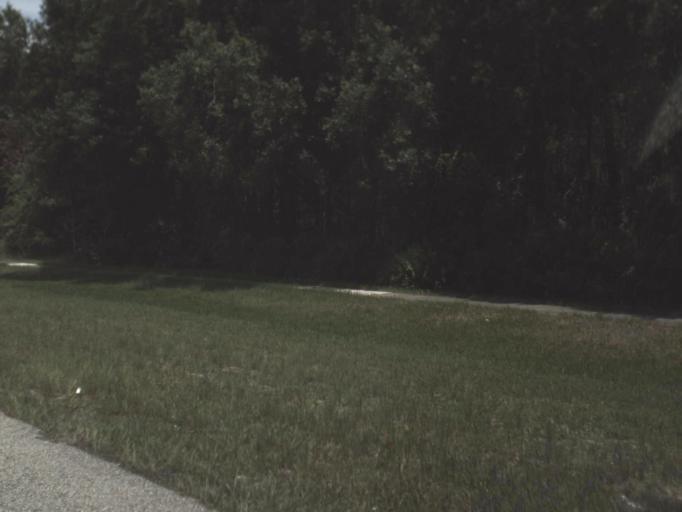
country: US
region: Florida
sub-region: Pasco County
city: Trinity
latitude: 28.1676
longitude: -82.6983
